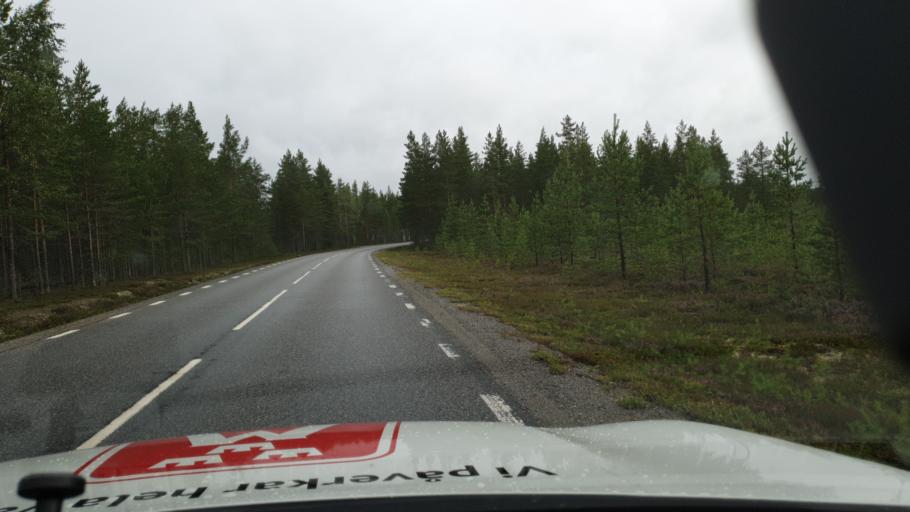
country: SE
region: Vaesterbotten
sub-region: Umea Kommun
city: Saevar
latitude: 63.9744
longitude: 20.5056
